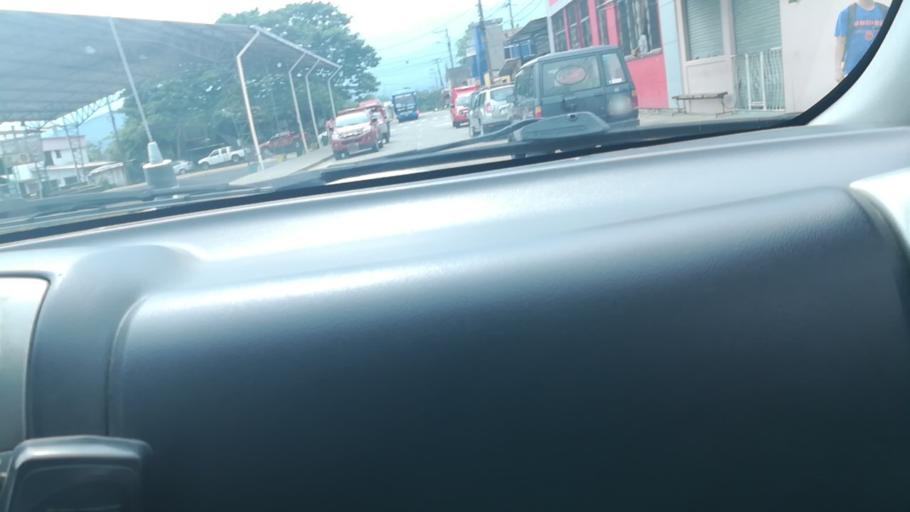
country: EC
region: Napo
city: Tena
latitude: -0.9874
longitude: -77.8205
